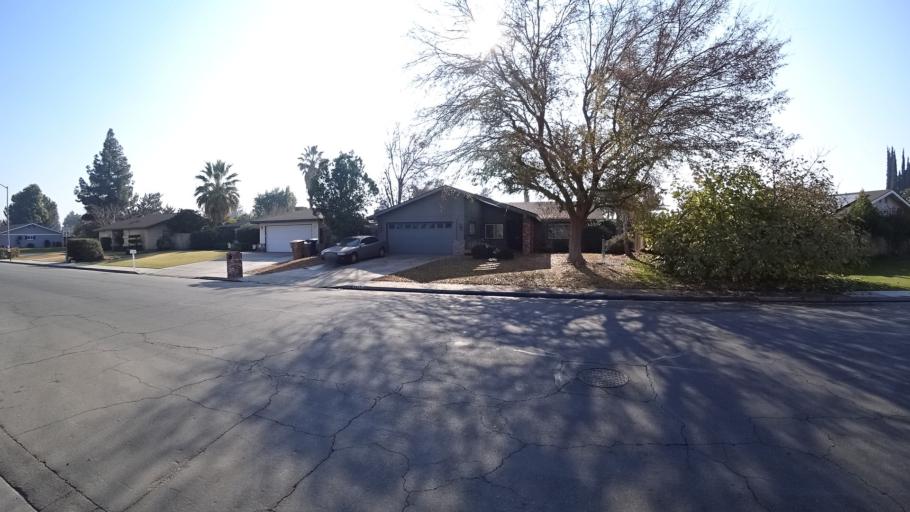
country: US
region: California
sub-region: Kern County
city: Greenacres
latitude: 35.3572
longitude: -119.0799
